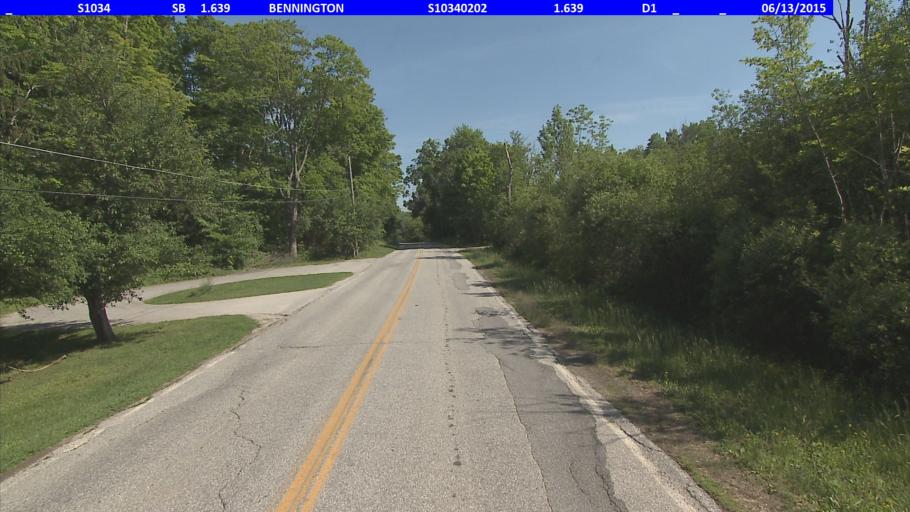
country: US
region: Vermont
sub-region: Bennington County
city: Bennington
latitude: 42.8739
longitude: -73.2132
